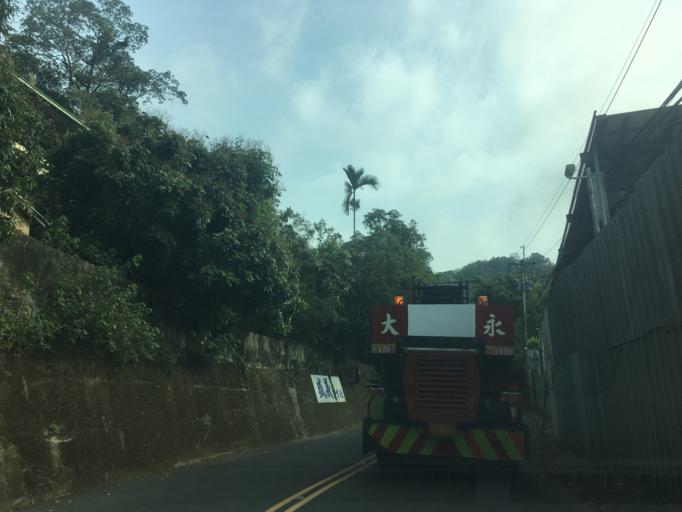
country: TW
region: Taiwan
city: Fengyuan
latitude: 24.2290
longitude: 120.7532
